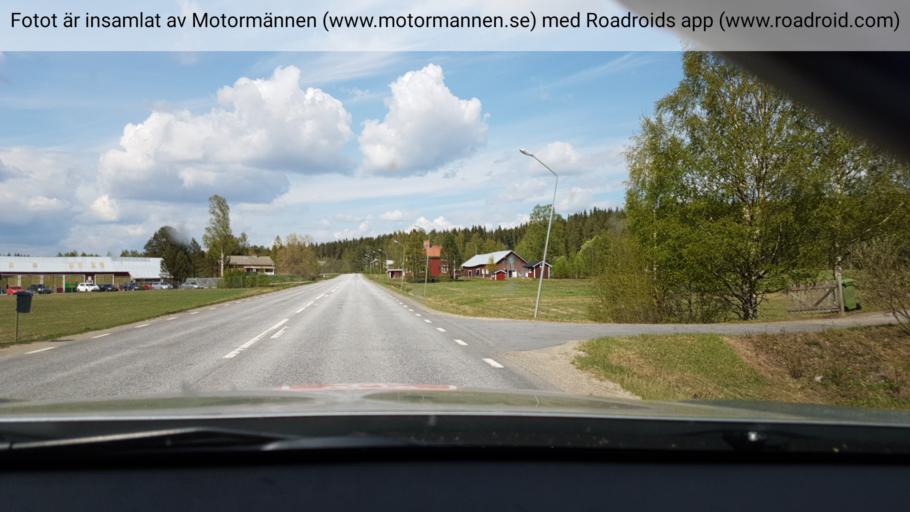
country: SE
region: Vaesterbotten
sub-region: Vannas Kommun
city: Vaennaes
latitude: 63.9603
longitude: 19.7529
